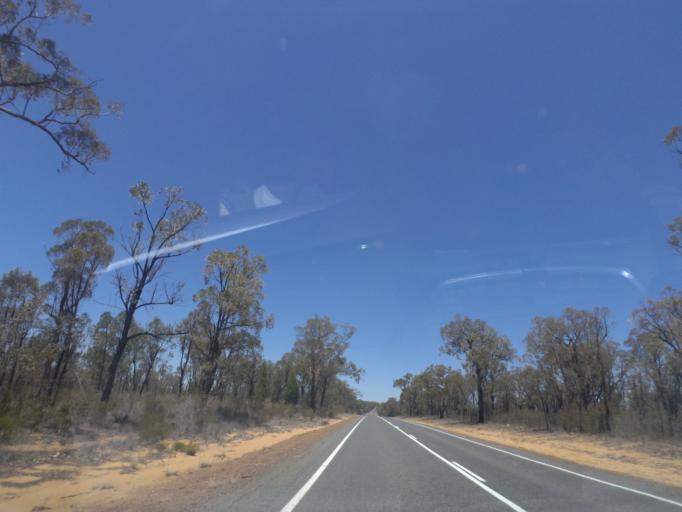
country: AU
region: New South Wales
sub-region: Narrabri
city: Narrabri
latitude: -30.7162
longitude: 149.5276
